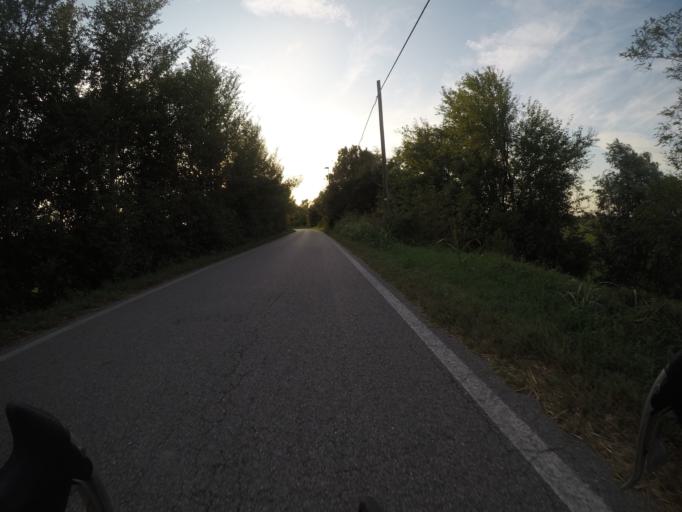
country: IT
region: Veneto
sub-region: Provincia di Rovigo
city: Pincara
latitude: 45.0029
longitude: 11.6155
